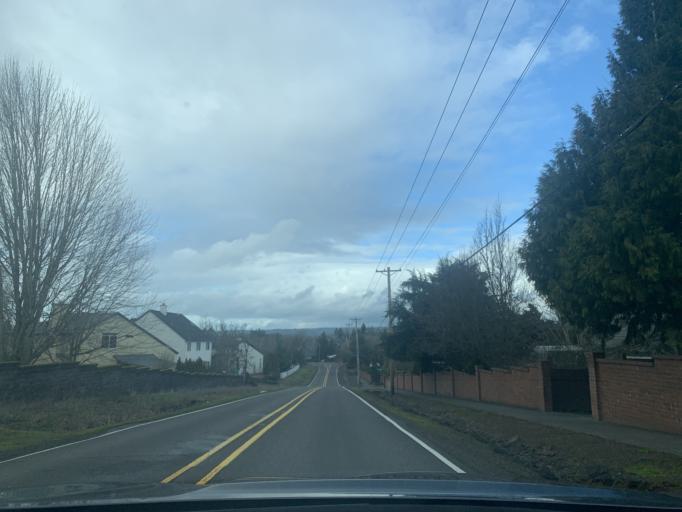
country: US
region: Oregon
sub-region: Washington County
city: Oak Hills
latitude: 45.5573
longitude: -122.8305
